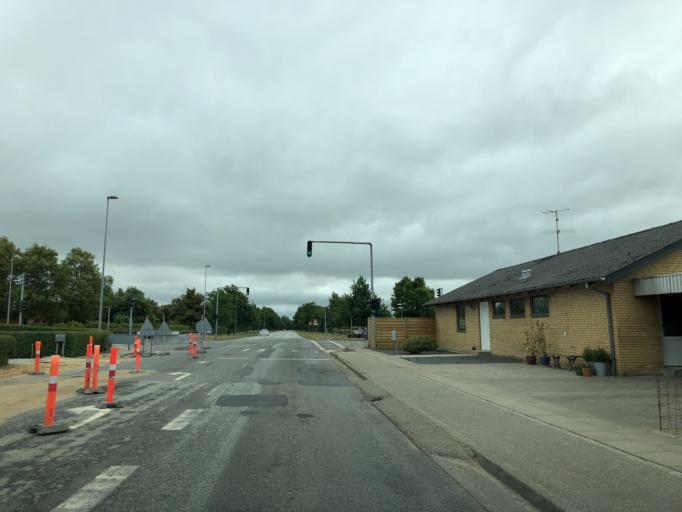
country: DK
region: Central Jutland
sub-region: Herning Kommune
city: Vildbjerg
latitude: 56.1935
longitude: 8.7600
